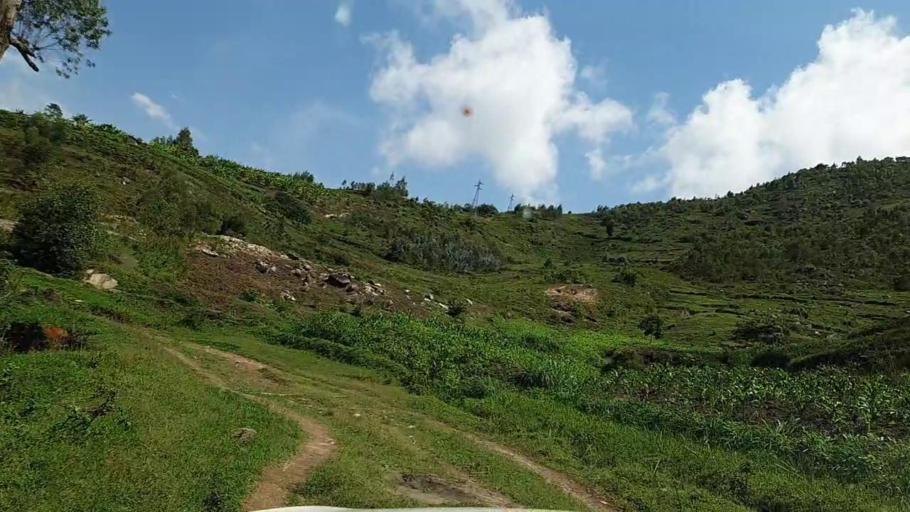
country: RW
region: Southern Province
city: Gikongoro
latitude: -2.3635
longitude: 29.5324
